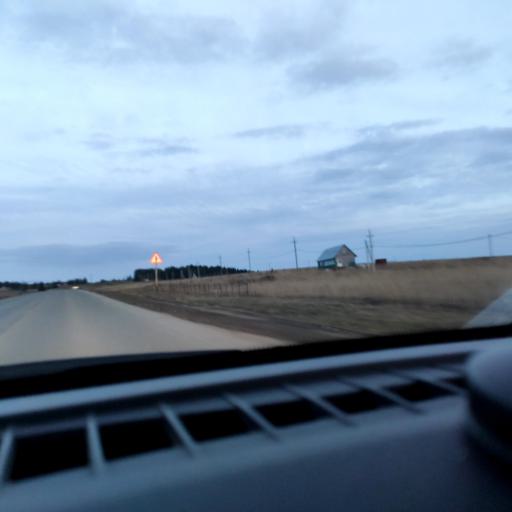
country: RU
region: Perm
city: Kultayevo
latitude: 57.8953
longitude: 55.7924
